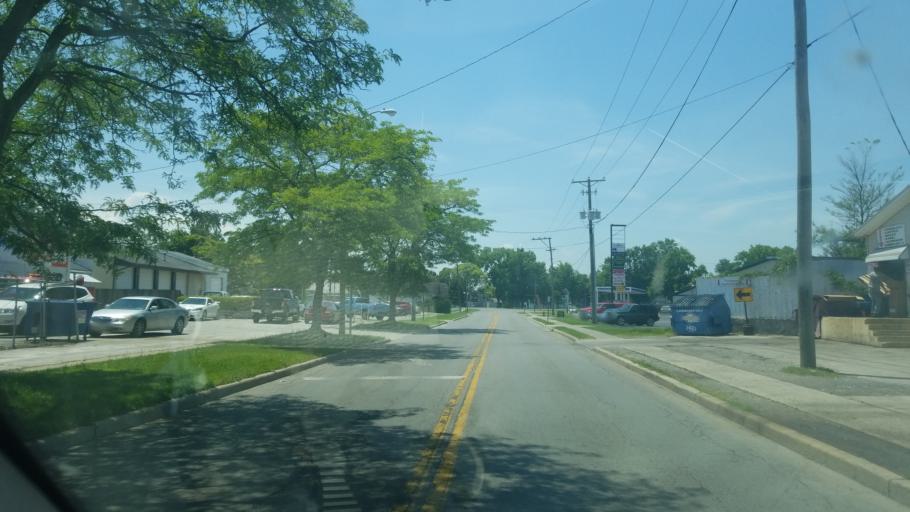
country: US
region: Ohio
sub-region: Hancock County
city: Findlay
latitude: 41.0483
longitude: -83.6457
